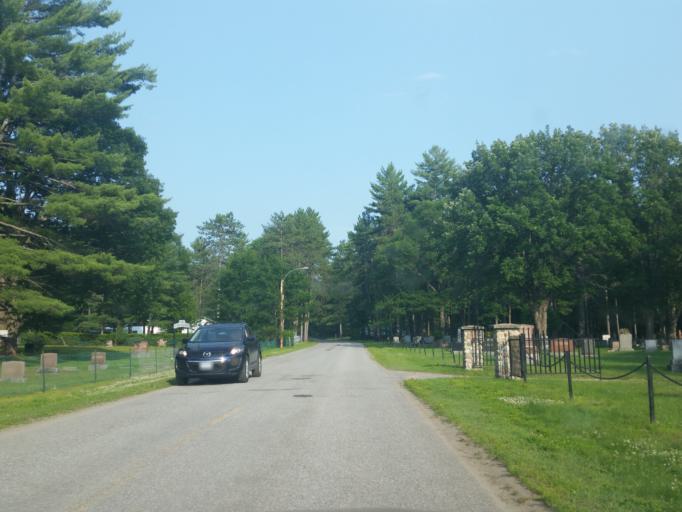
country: CA
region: Quebec
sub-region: Outaouais
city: Shawville
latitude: 45.5204
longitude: -76.4211
